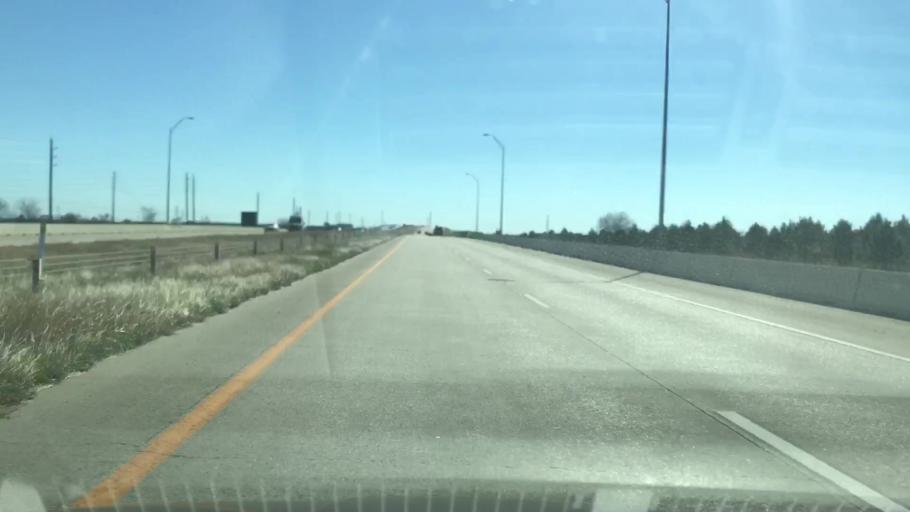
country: US
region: Texas
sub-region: Harris County
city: Cypress
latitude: 29.9284
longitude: -95.7629
